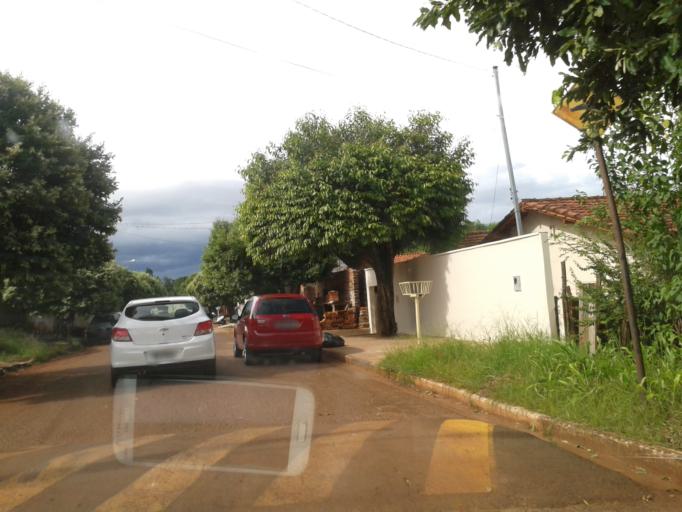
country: BR
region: Minas Gerais
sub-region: Ituiutaba
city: Ituiutaba
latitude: -18.9815
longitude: -49.4738
